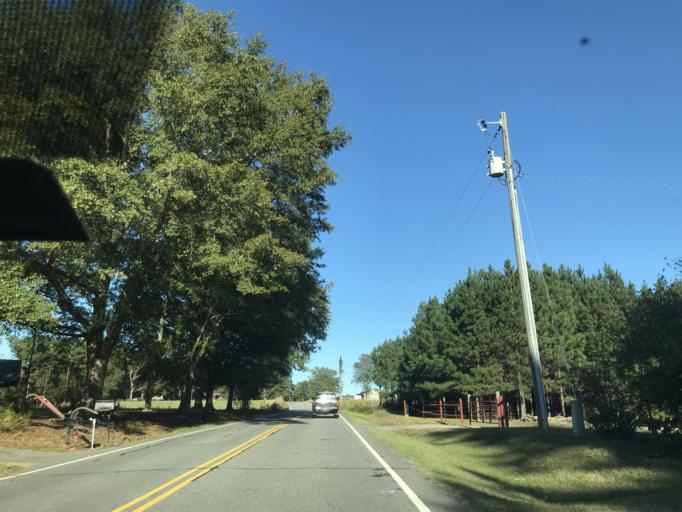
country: US
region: South Carolina
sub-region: Spartanburg County
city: Mayo
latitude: 35.1115
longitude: -81.8260
